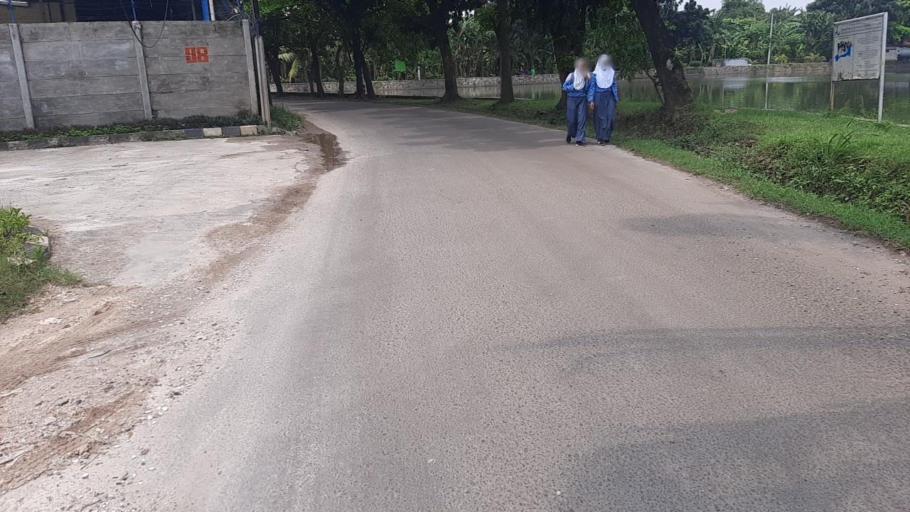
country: ID
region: West Java
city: Cileungsir
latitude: -6.4254
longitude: 106.9345
